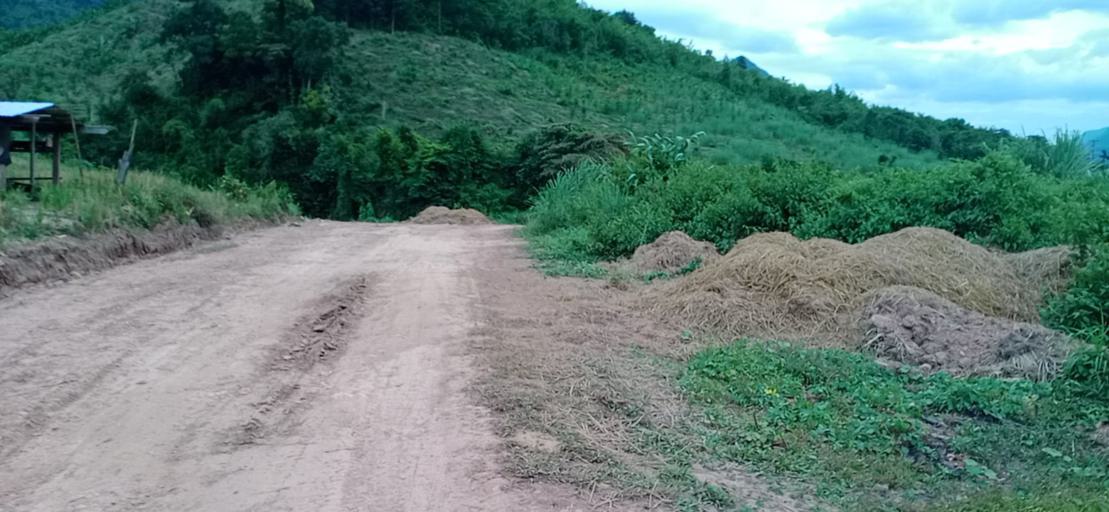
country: TH
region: Changwat Bueng Kan
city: Pak Khat
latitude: 18.5526
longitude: 103.1642
